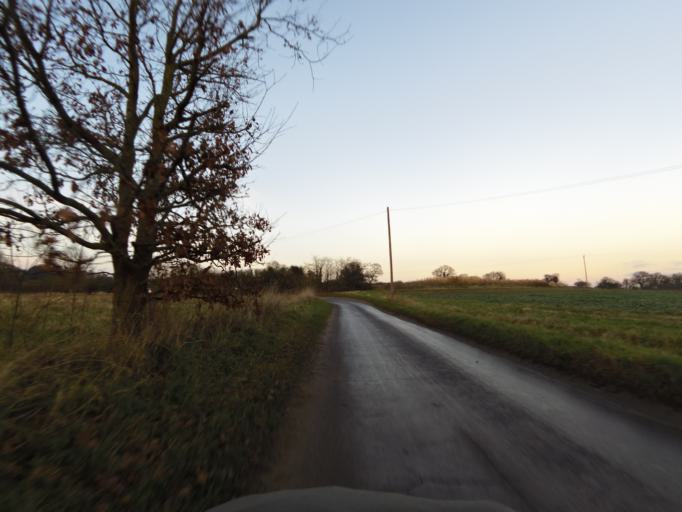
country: GB
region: England
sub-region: Norfolk
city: Sheringham
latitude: 52.8963
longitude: 1.2222
